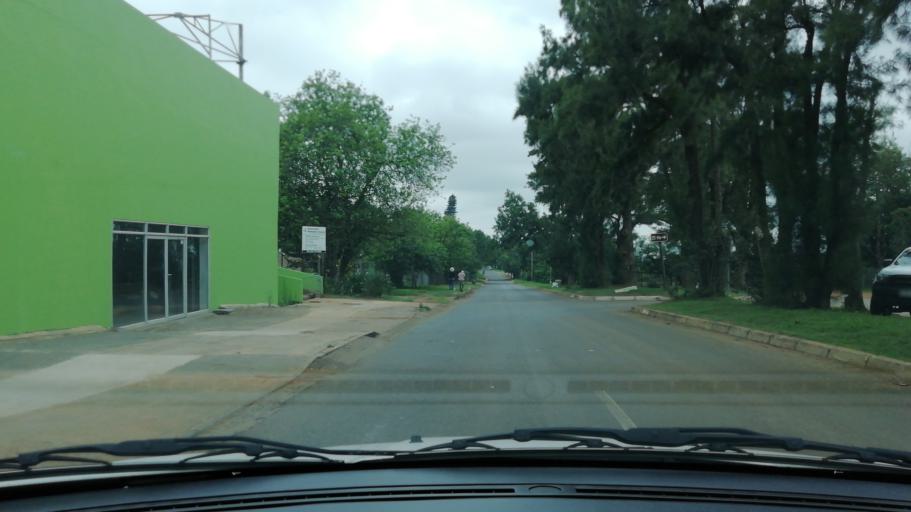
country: ZA
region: KwaZulu-Natal
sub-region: uThungulu District Municipality
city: Empangeni
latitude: -28.7451
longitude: 31.8919
